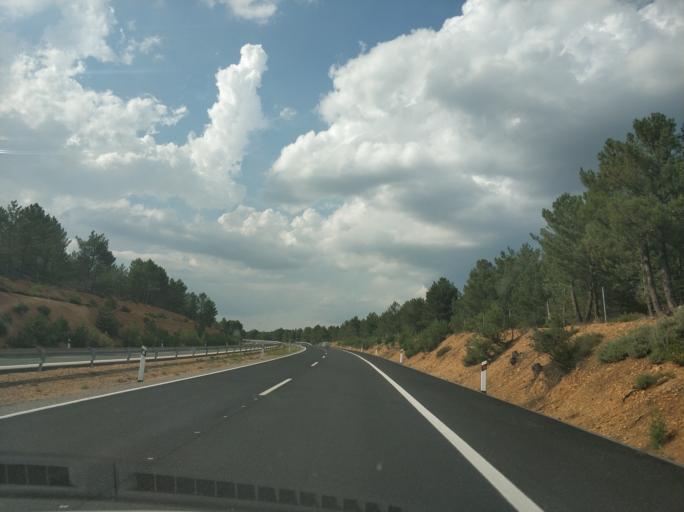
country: ES
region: Castille and Leon
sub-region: Provincia de Leon
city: Cimanes del Tejar
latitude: 42.6423
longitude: -5.7448
